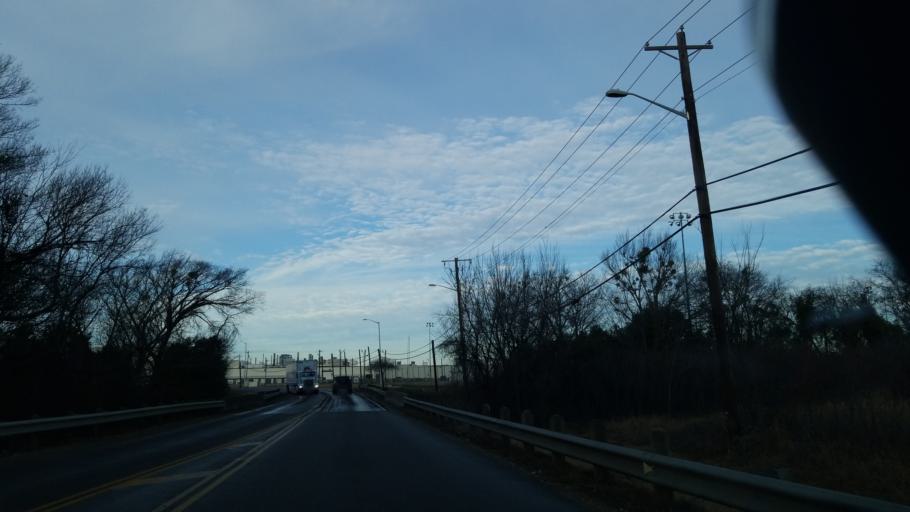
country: US
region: Texas
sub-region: Denton County
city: Denton
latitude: 33.2043
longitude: -97.1710
